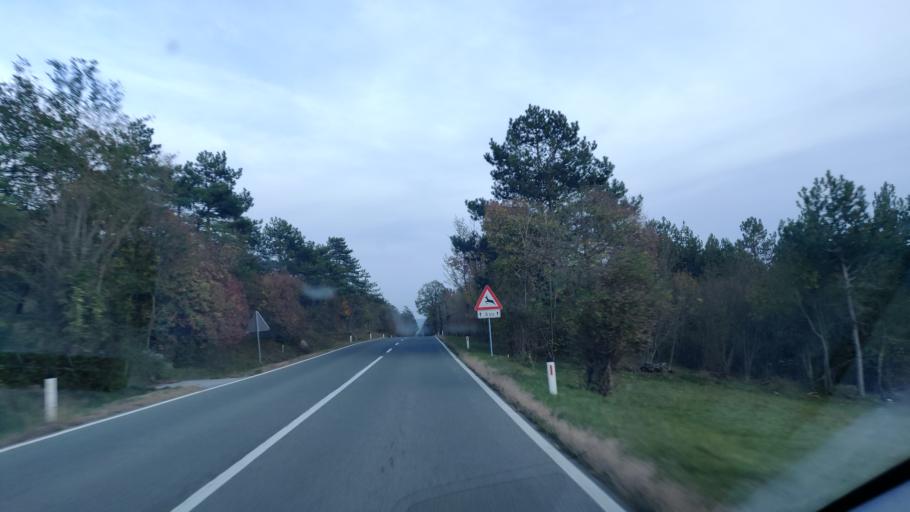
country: SI
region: Divaca
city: Divaca
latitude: 45.7313
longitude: 13.9605
